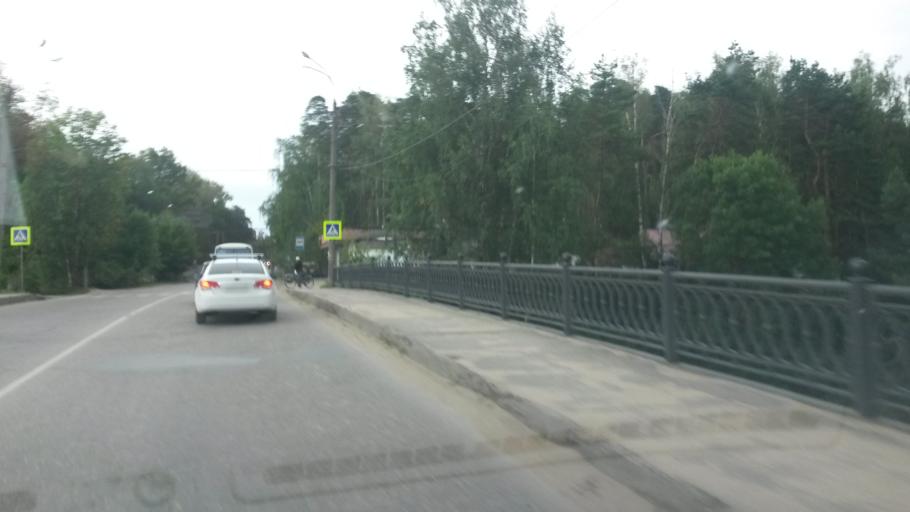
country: RU
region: Ivanovo
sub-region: Gorod Ivanovo
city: Ivanovo
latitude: 57.0262
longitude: 40.9378
